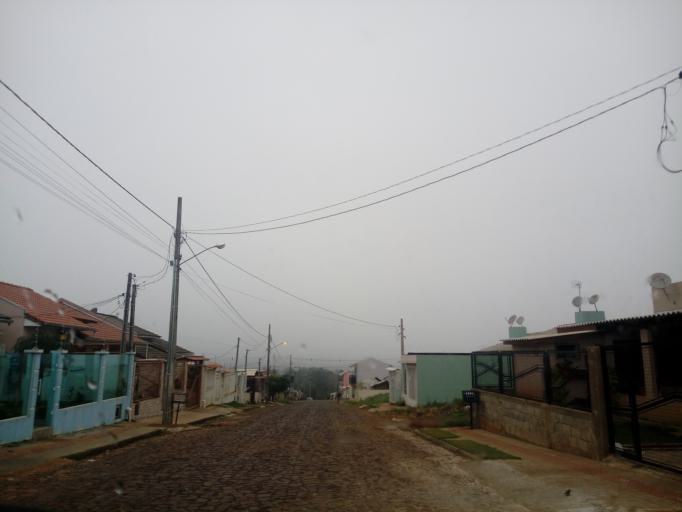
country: BR
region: Santa Catarina
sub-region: Chapeco
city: Chapeco
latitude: -27.1080
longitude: -52.6719
